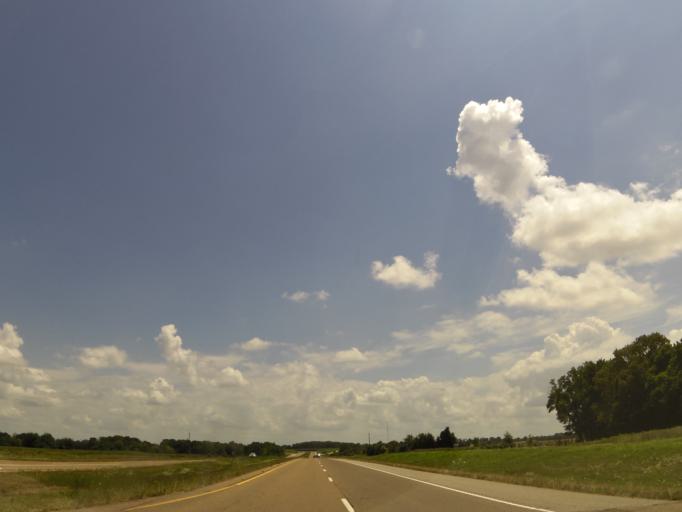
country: US
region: Tennessee
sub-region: Crockett County
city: Alamo
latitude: 35.8095
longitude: -89.1608
